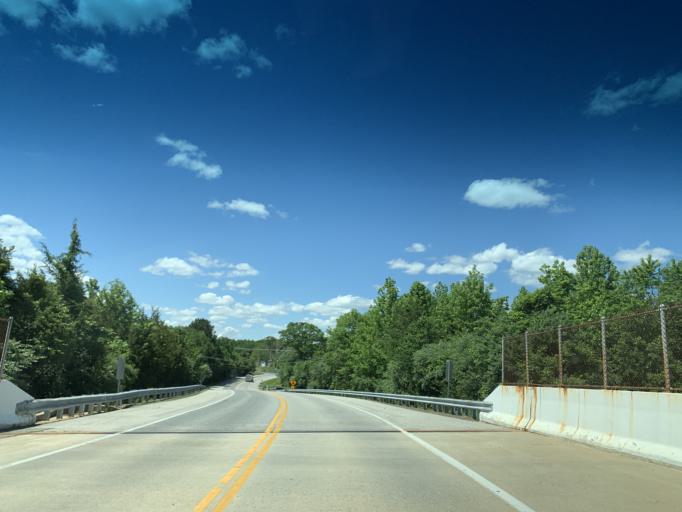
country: US
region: Maryland
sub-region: Cecil County
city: Elkton
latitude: 39.6030
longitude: -75.8600
